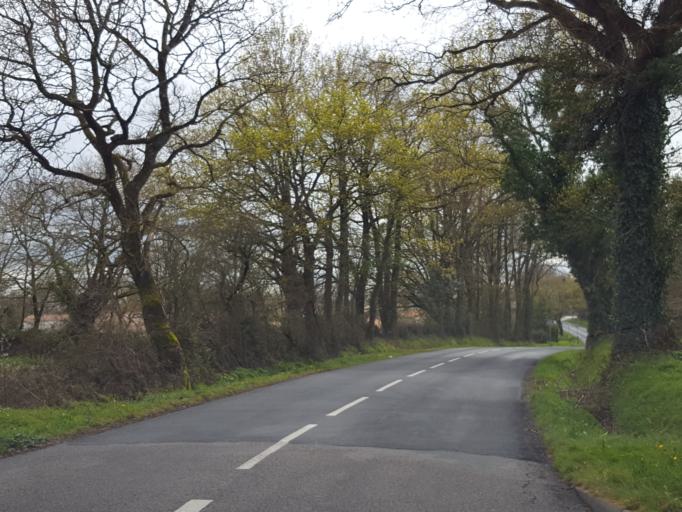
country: FR
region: Pays de la Loire
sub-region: Departement de la Vendee
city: La Roche-sur-Yon
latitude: 46.6707
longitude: -1.3978
